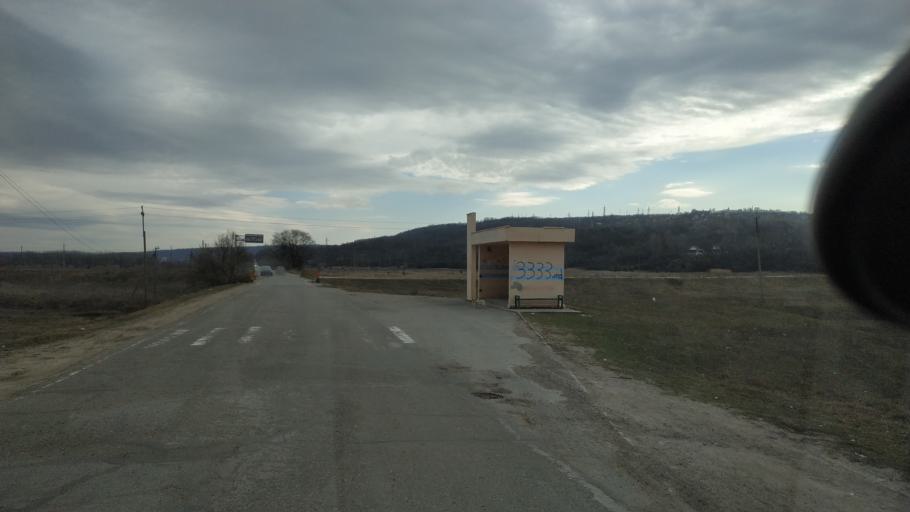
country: MD
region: Chisinau
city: Vadul lui Voda
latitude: 47.1167
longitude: 29.0564
